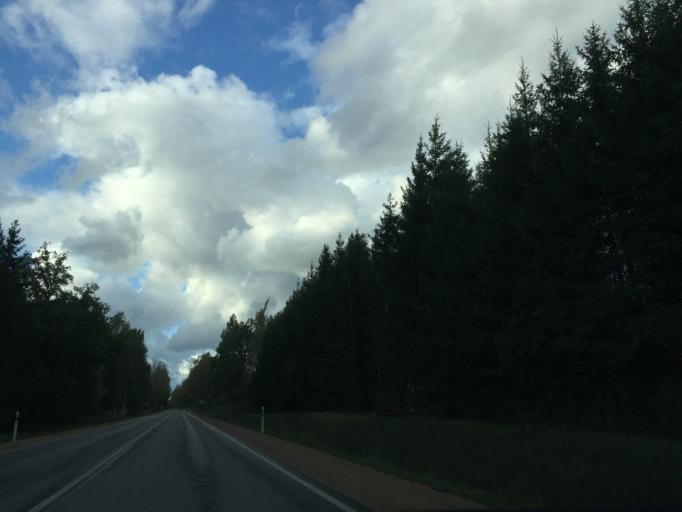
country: LV
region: Ligatne
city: Ligatne
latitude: 57.1766
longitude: 25.0399
